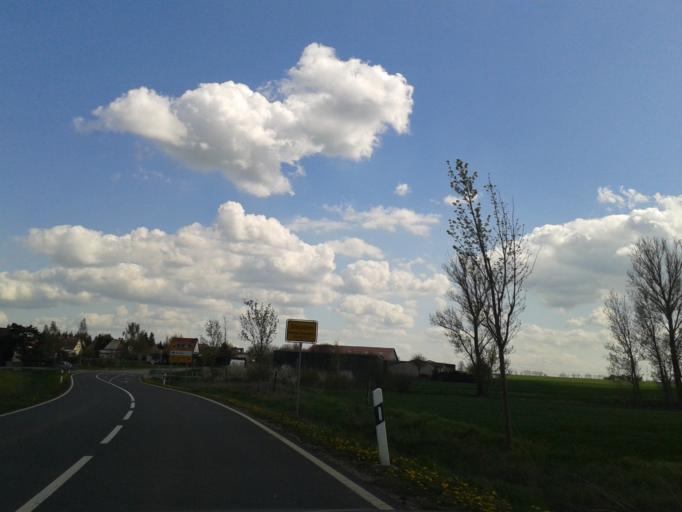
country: DE
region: Saxony-Anhalt
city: Schafstadt
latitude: 51.4183
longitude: 11.7603
